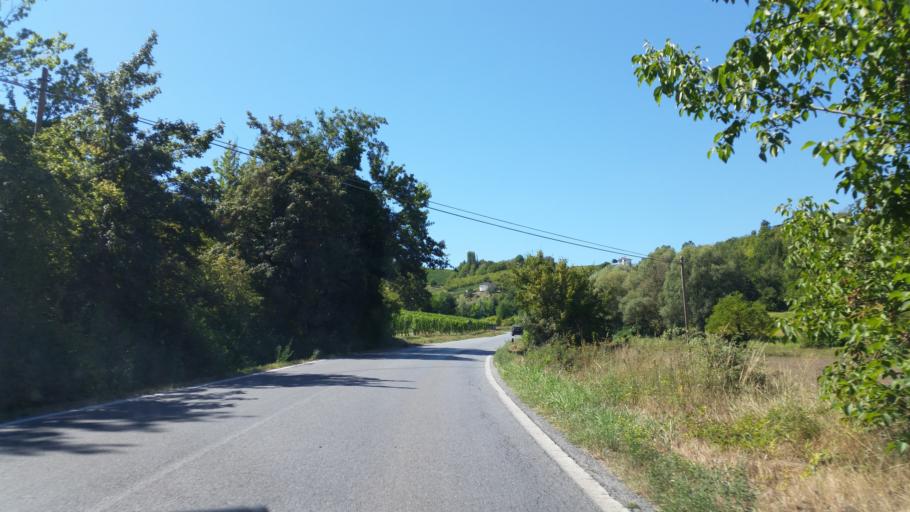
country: IT
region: Piedmont
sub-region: Provincia di Cuneo
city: Alba
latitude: 44.6958
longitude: 8.0540
